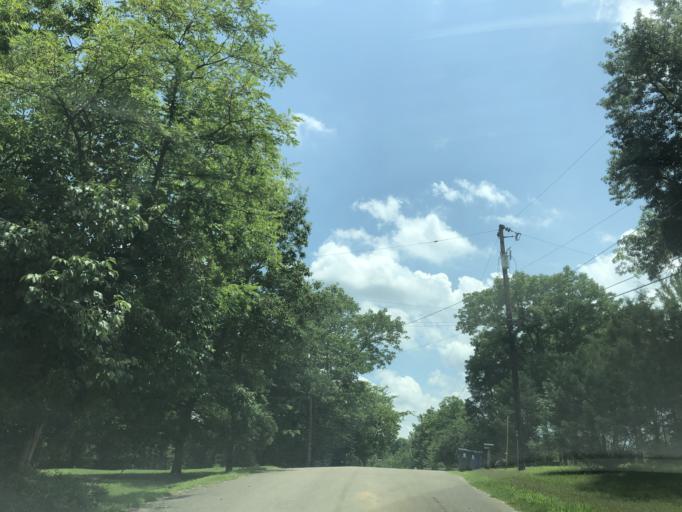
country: US
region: Tennessee
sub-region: Williamson County
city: Brentwood Estates
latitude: 36.0098
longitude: -86.7167
